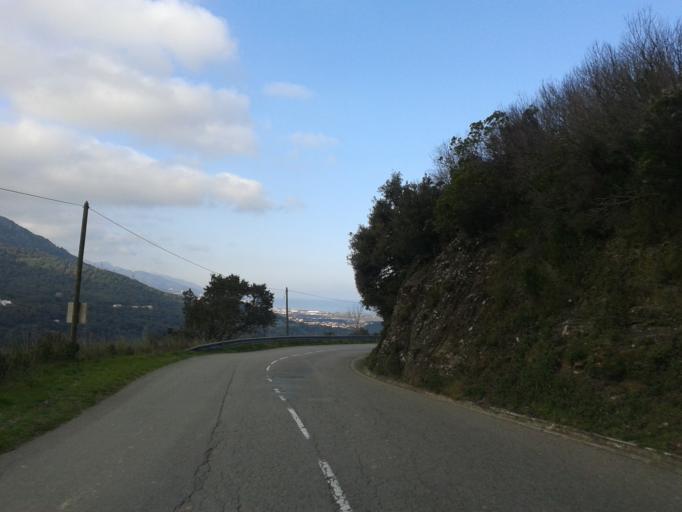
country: FR
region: Corsica
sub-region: Departement de la Haute-Corse
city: Biguglia
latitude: 42.5978
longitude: 9.4126
